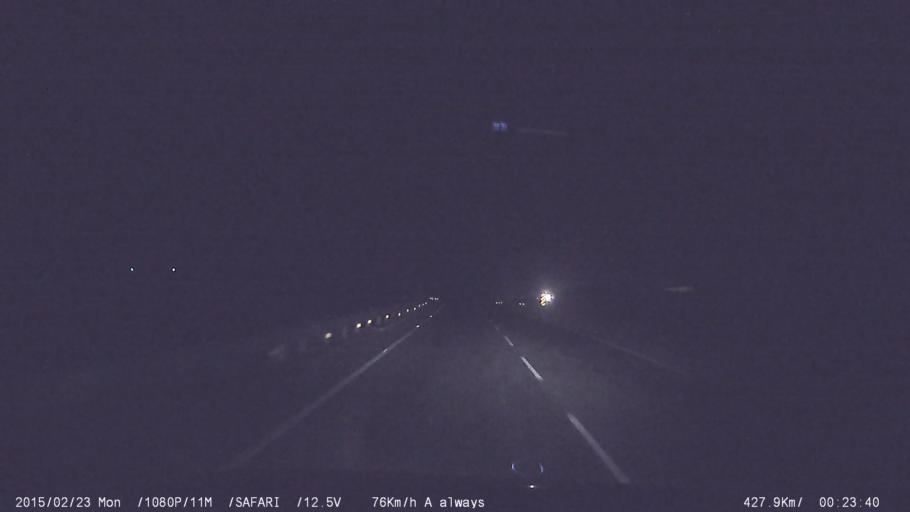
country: IN
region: Tamil Nadu
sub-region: Salem
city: Omalur
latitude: 11.9266
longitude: 78.0652
